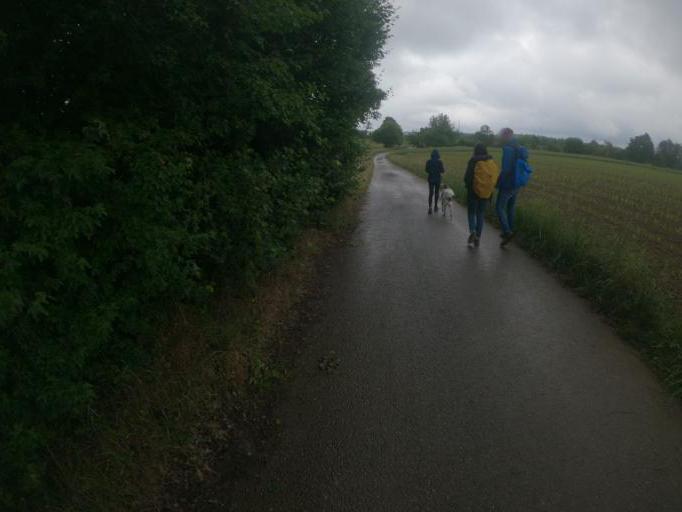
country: DE
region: Baden-Wuerttemberg
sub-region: Regierungsbezirk Stuttgart
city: Adelberg
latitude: 48.7663
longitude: 9.5931
